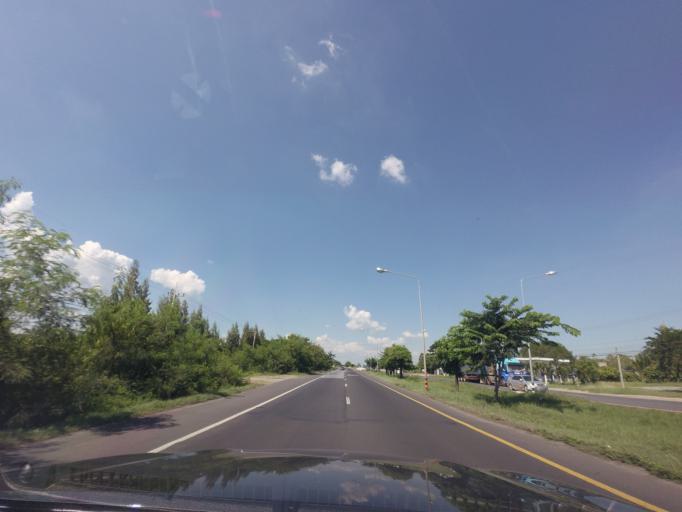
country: TH
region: Nakhon Ratchasima
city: Non Sung
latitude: 15.1980
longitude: 102.3506
